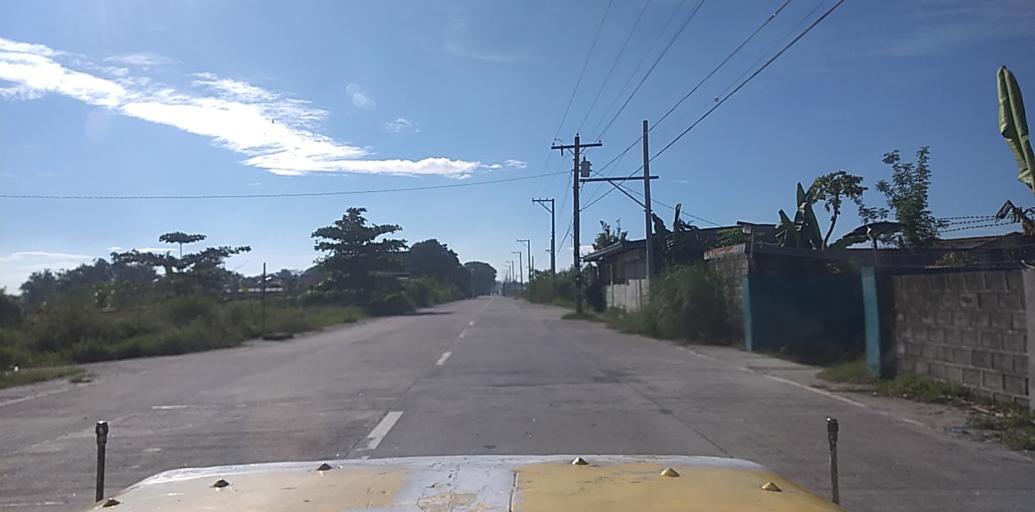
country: PH
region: Central Luzon
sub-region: Province of Pampanga
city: Anao
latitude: 15.1329
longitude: 120.6963
